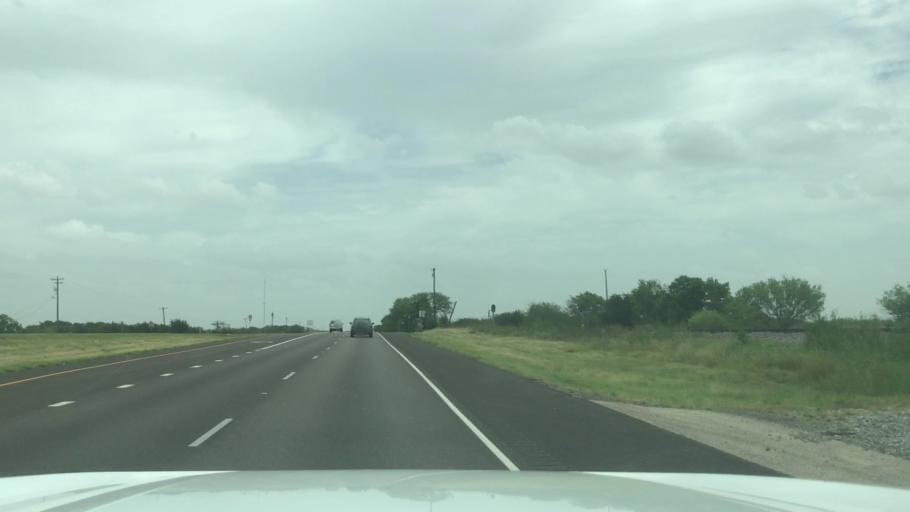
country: US
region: Texas
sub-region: McLennan County
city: Riesel
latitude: 31.5193
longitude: -96.9786
